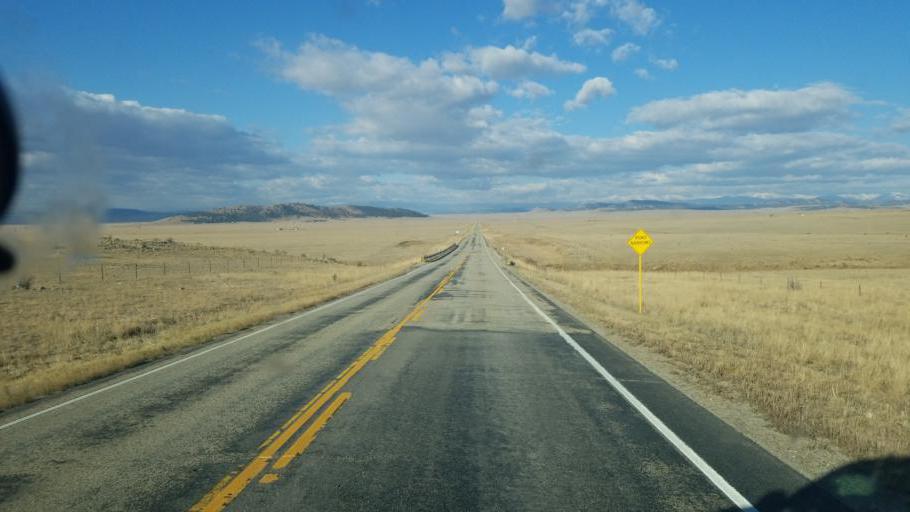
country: US
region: Colorado
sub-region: Park County
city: Fairplay
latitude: 39.0479
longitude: -105.5683
